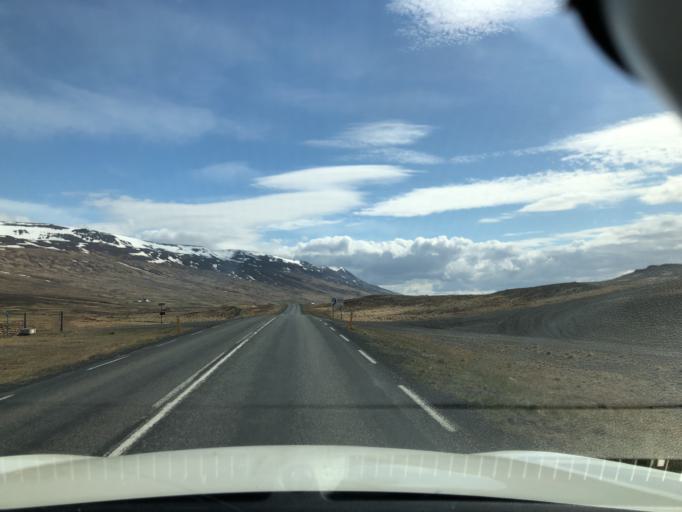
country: IS
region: Northwest
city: Saudarkrokur
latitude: 65.6635
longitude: -20.2273
